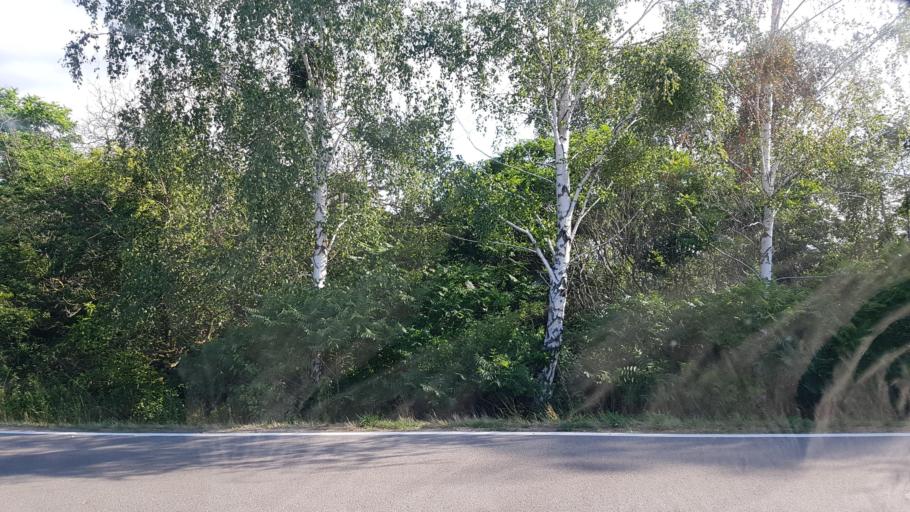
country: DE
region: Brandenburg
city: Grossraschen
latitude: 51.5763
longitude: 14.0223
